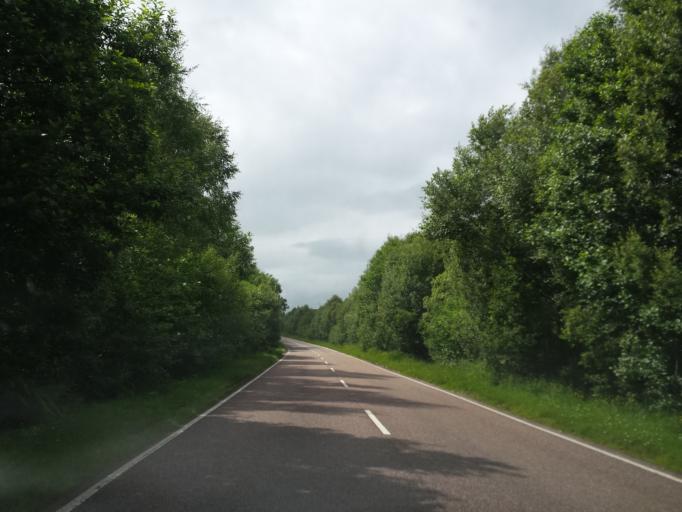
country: GB
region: Scotland
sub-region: Highland
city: Fort William
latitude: 56.8562
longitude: -5.2906
